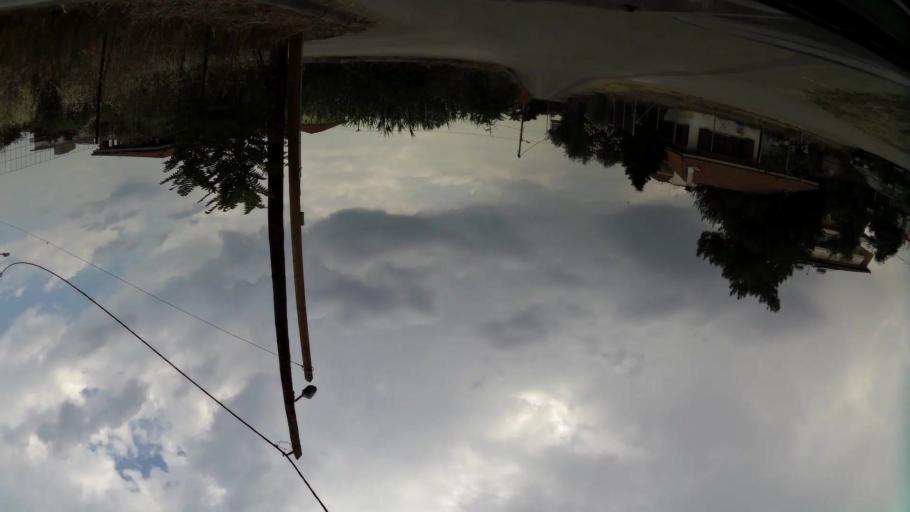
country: GR
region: Central Macedonia
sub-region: Nomos Imathias
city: Veroia
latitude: 40.5333
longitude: 22.2095
